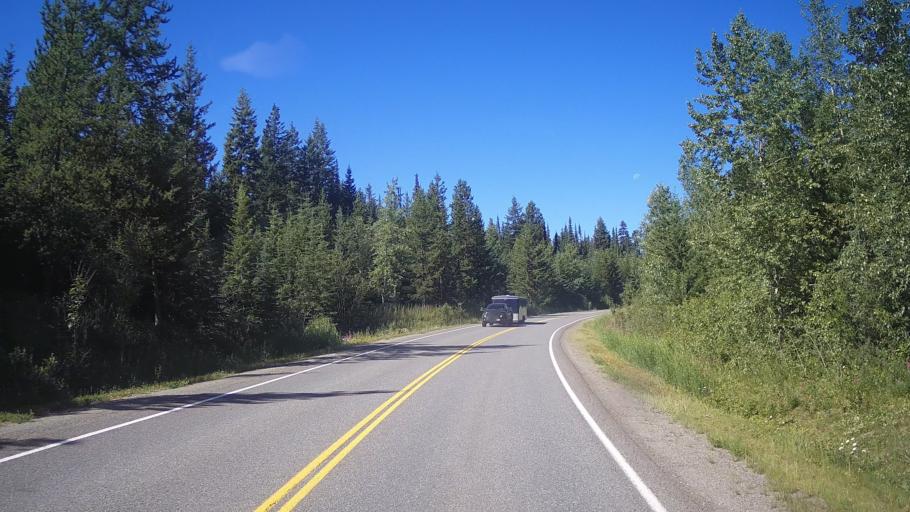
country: CA
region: British Columbia
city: Kamloops
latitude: 51.4986
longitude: -120.3617
